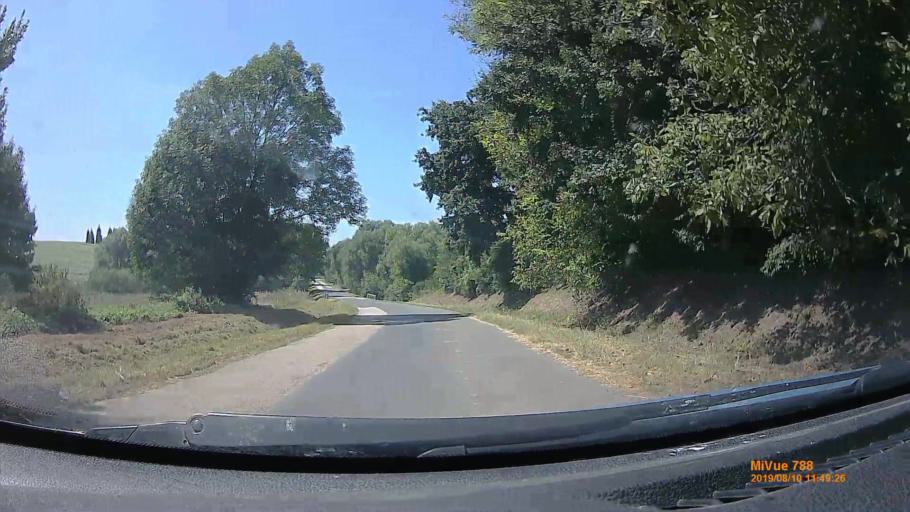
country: HU
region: Somogy
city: Somogyvar
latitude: 46.4976
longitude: 17.7287
